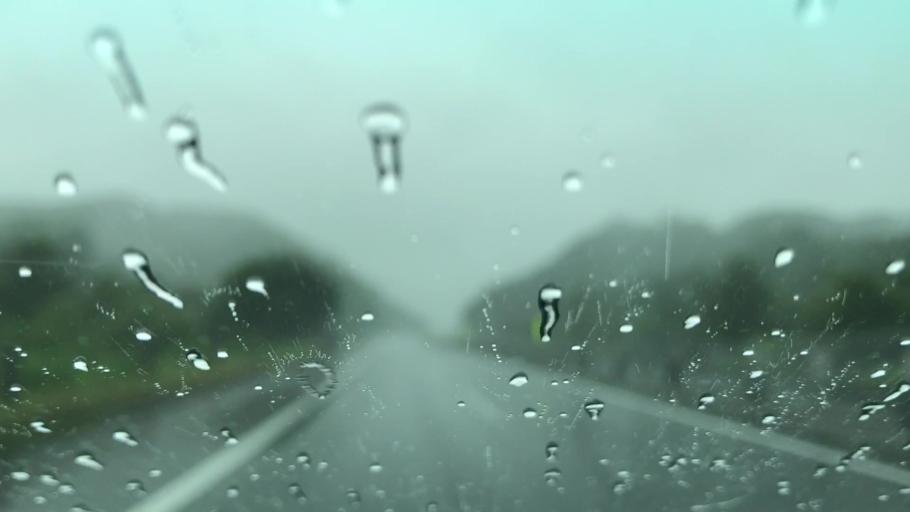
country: JP
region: Hokkaido
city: Shiraoi
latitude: 42.5582
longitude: 141.3170
